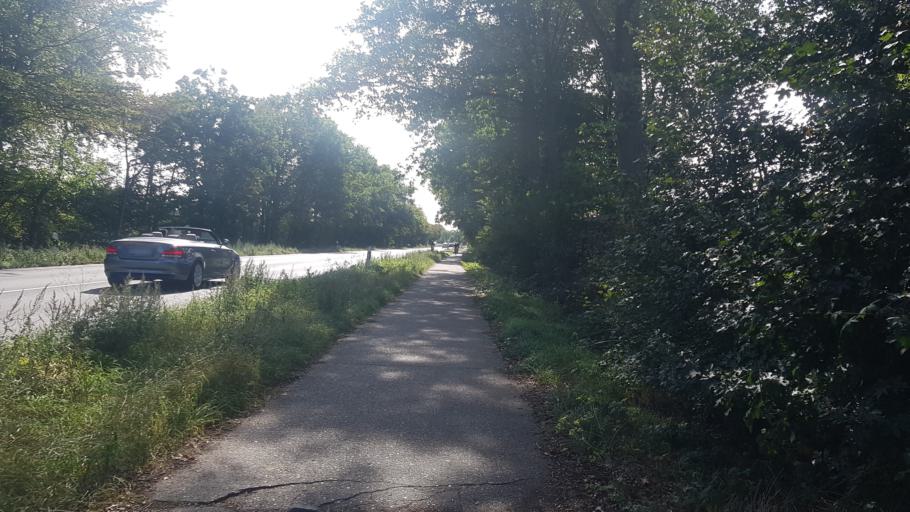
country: DE
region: North Rhine-Westphalia
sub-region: Regierungsbezirk Dusseldorf
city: Ratingen
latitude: 51.3194
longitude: 6.8310
